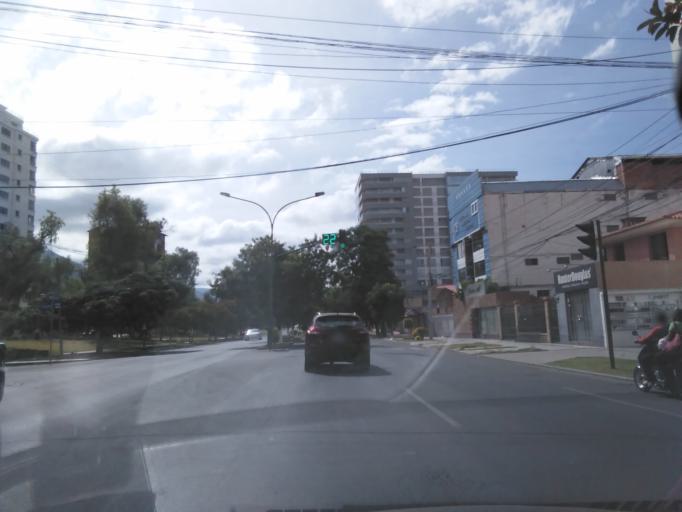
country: BO
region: Cochabamba
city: Cochabamba
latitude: -17.3736
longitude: -66.1470
